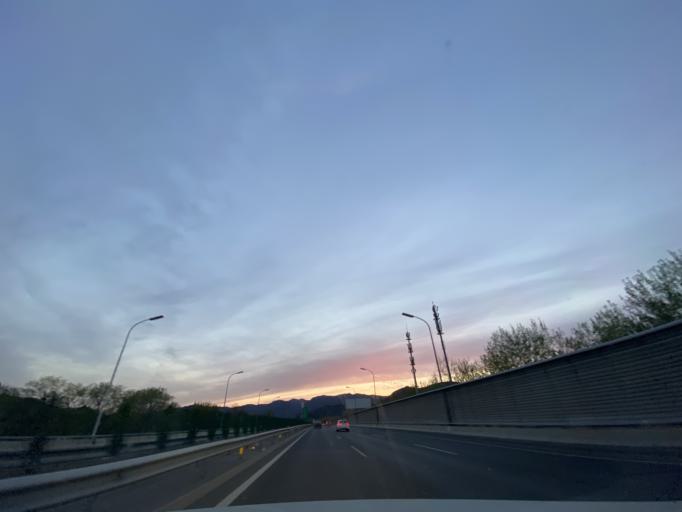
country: CN
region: Beijing
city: Haidian
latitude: 40.0018
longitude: 116.2539
